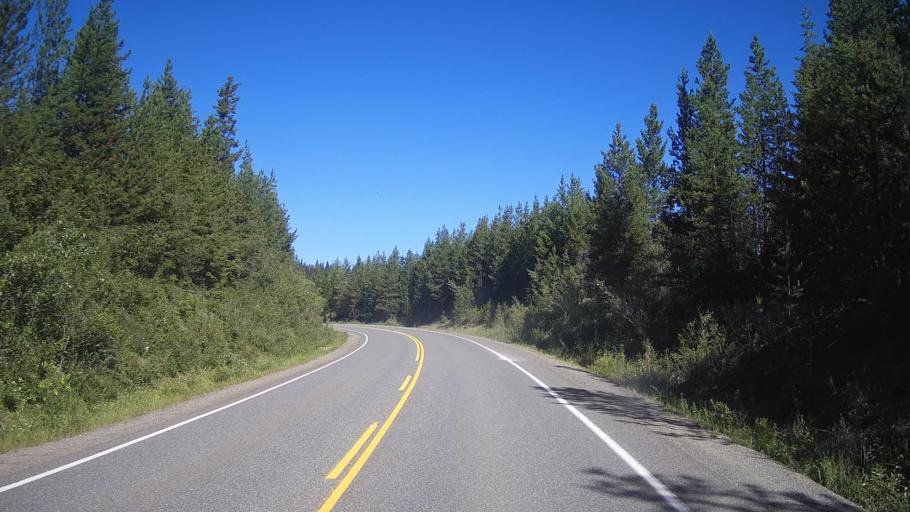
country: CA
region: British Columbia
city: Kamloops
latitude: 51.5028
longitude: -120.3483
